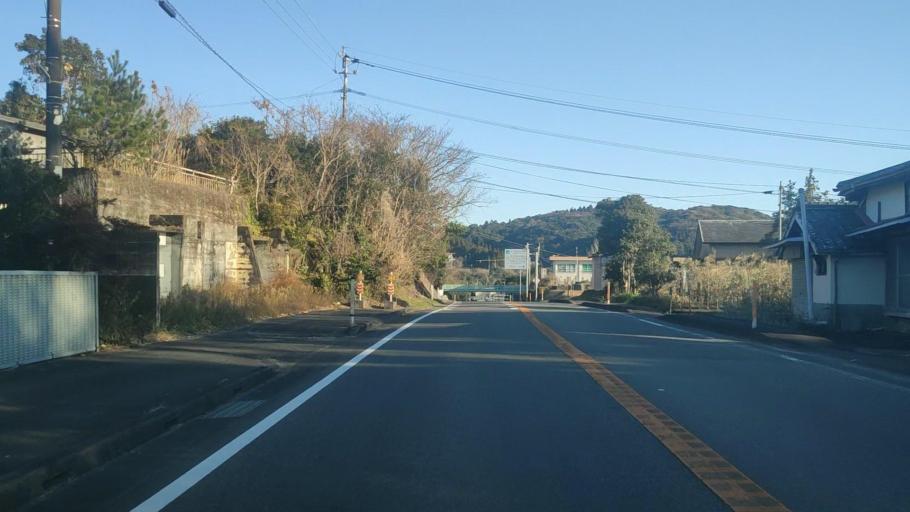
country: JP
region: Miyazaki
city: Takanabe
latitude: 32.3359
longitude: 131.6102
